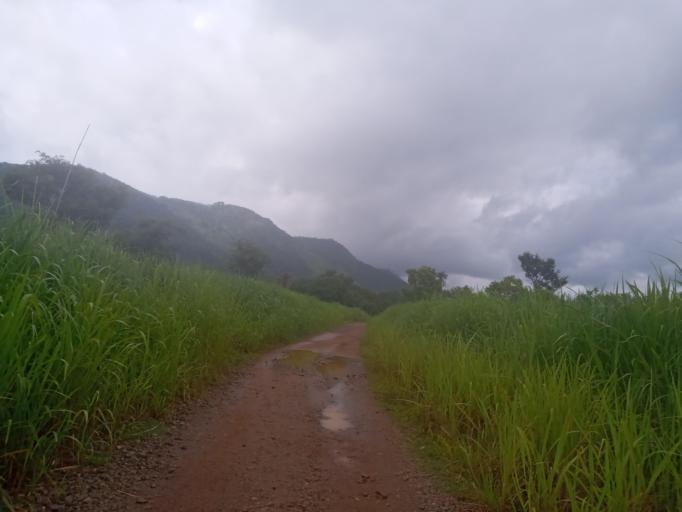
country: SL
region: Northern Province
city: Bumbuna
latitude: 8.9476
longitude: -11.7532
